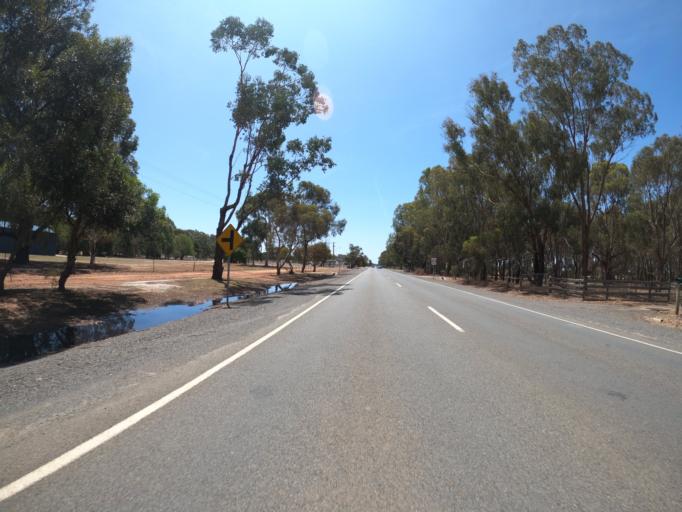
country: AU
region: Victoria
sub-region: Moira
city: Yarrawonga
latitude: -36.0370
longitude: 145.9955
